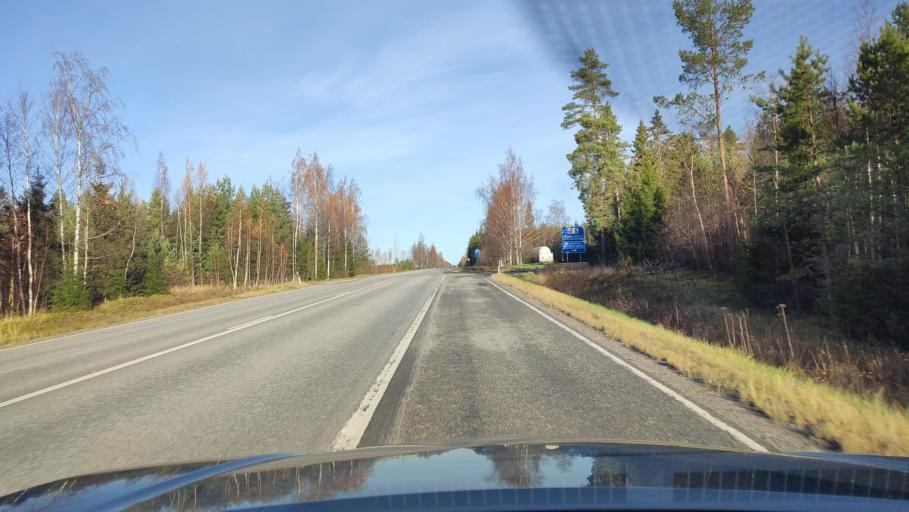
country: FI
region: Ostrobothnia
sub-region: Sydosterbotten
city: Naerpes
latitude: 62.5040
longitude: 21.4502
